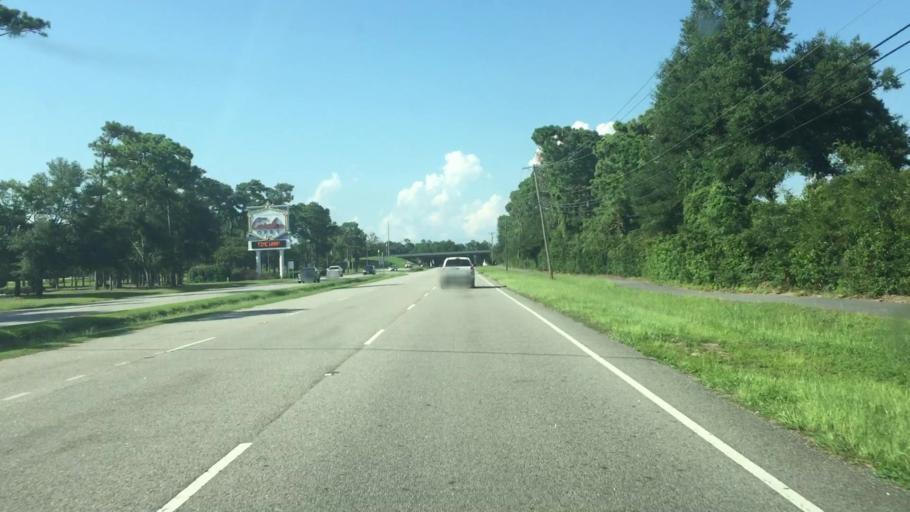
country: US
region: South Carolina
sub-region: Horry County
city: Myrtle Beach
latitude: 33.7634
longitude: -78.8060
